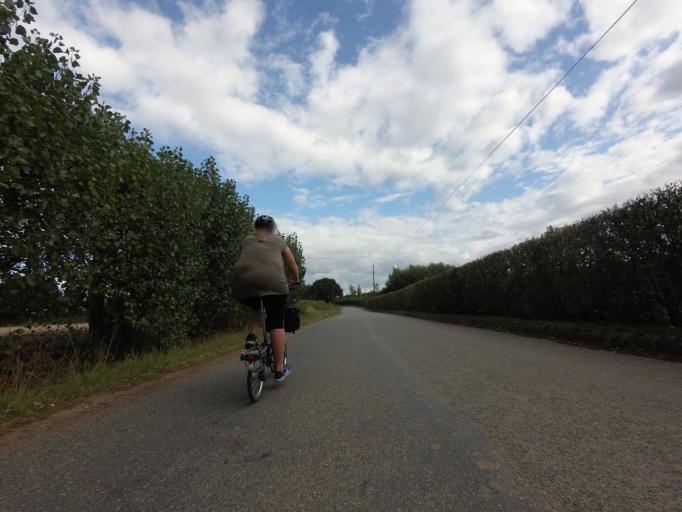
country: GB
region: England
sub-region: Kent
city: Marden
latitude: 51.2114
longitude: 0.4985
